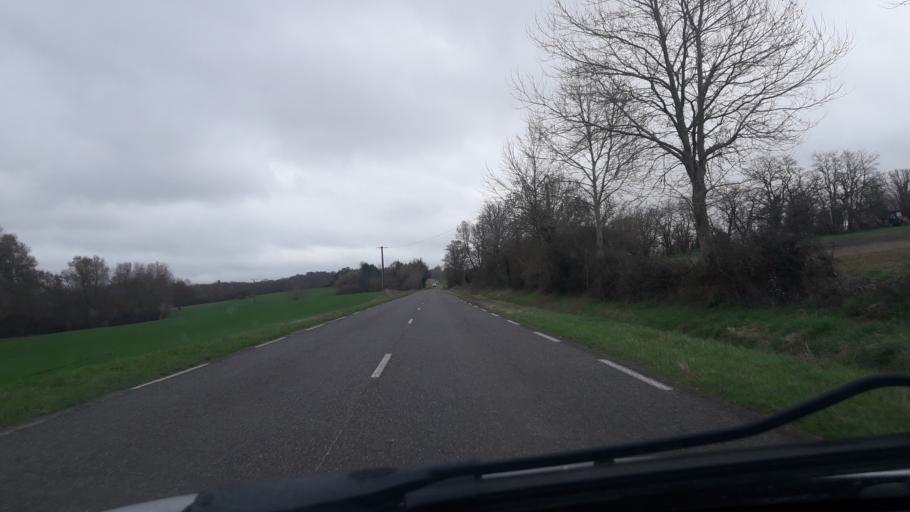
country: FR
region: Midi-Pyrenees
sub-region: Departement du Gers
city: Gimont
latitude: 43.6745
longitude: 1.0116
